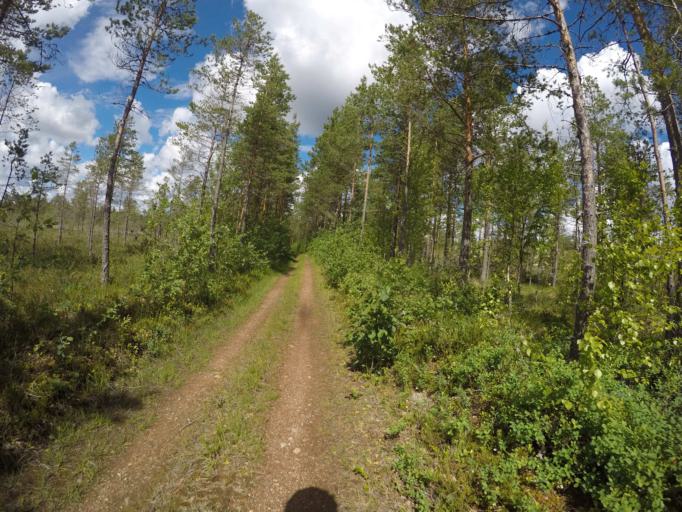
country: SE
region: Vaermland
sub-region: Filipstads Kommun
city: Lesjofors
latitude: 60.1420
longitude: 14.2830
